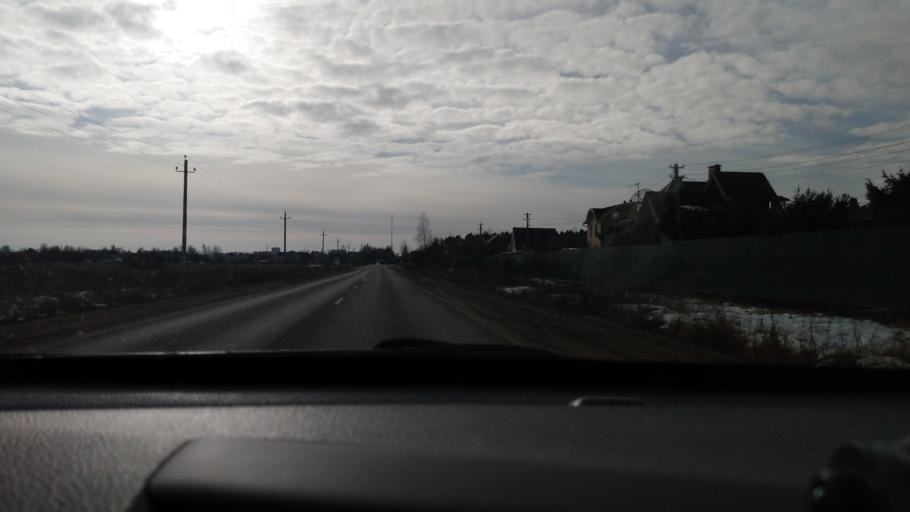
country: RU
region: Moskovskaya
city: Nakhabino
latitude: 55.8755
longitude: 37.1865
